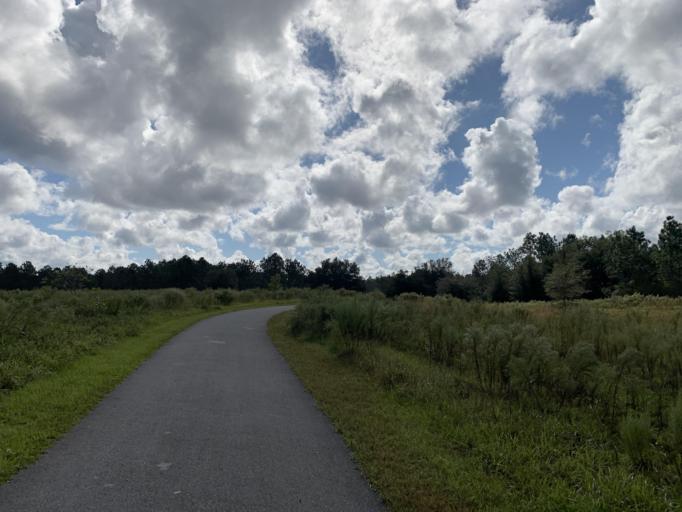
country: US
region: Florida
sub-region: Marion County
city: Silver Springs Shores
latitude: 29.1563
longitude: -82.0448
